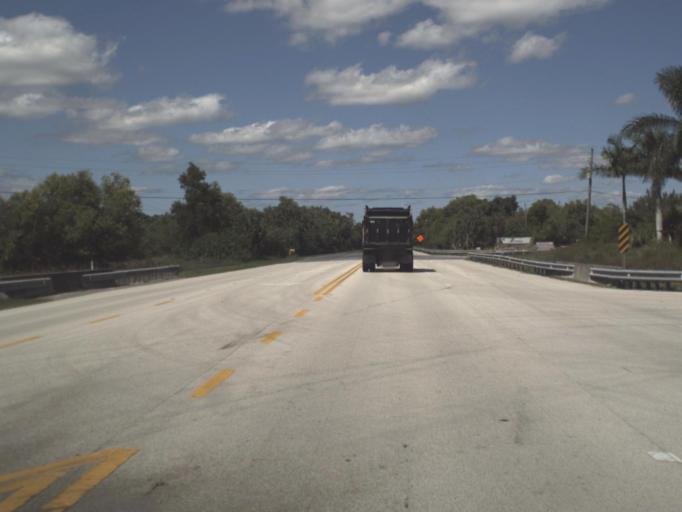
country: US
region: Florida
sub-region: Collier County
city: Lely Resort
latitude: 26.0252
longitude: -81.6396
